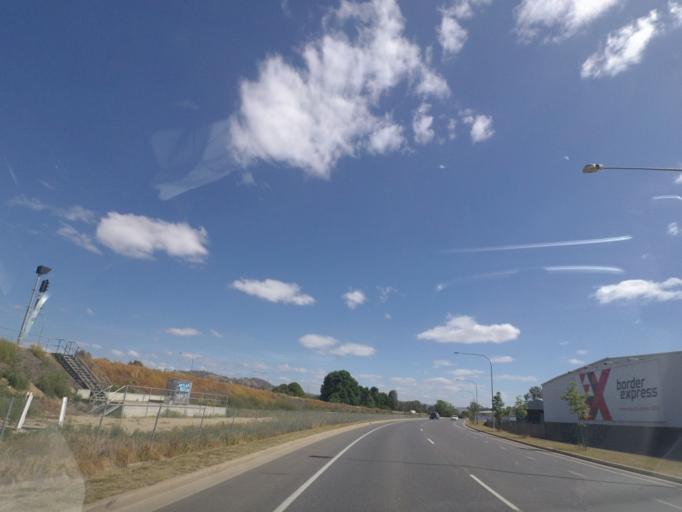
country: AU
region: New South Wales
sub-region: Albury Municipality
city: East Albury
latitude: -36.0919
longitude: 146.9226
